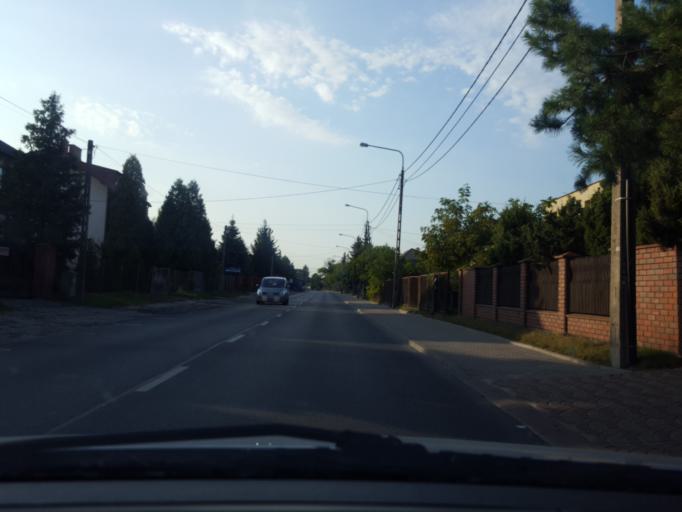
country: PL
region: Masovian Voivodeship
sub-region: Warszawa
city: Rembertow
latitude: 52.2649
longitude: 21.1559
